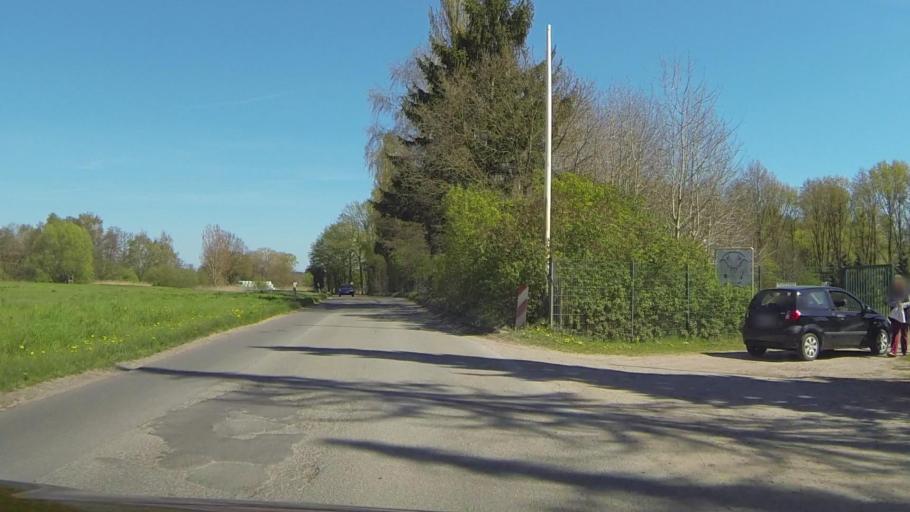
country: DE
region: Schleswig-Holstein
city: Tornesch
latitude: 53.6769
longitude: 9.7002
